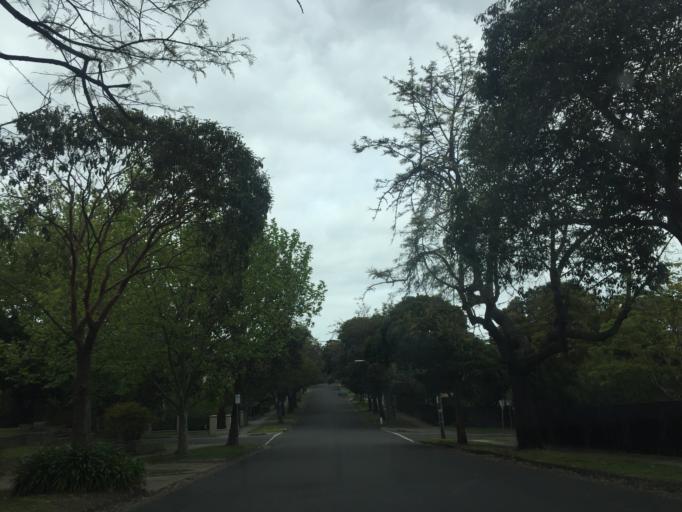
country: AU
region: Victoria
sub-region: Boroondara
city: Kew East
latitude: -37.8099
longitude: 145.0494
